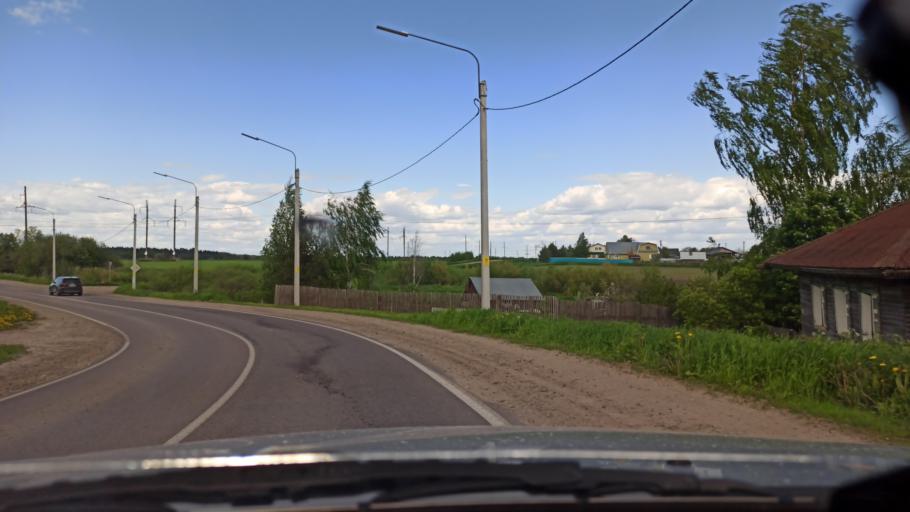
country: RU
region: Vologda
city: Vologda
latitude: 59.2901
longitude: 39.8550
